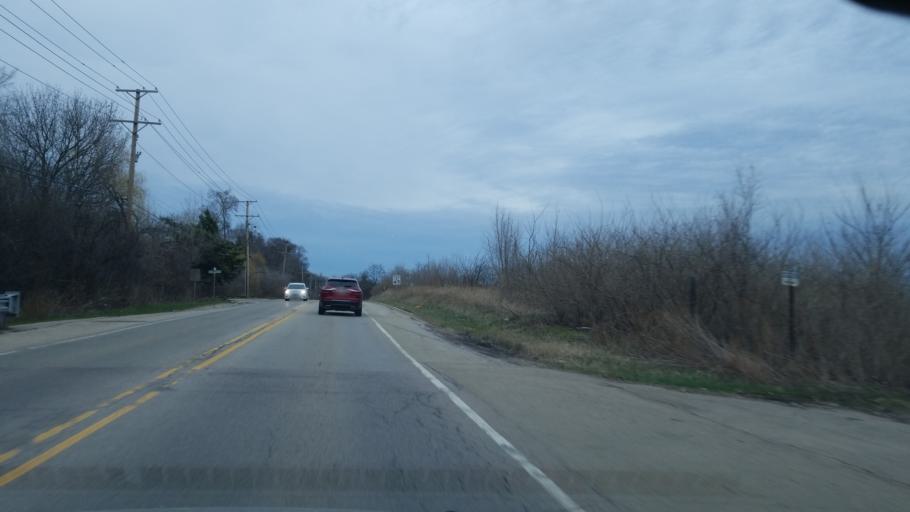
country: US
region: Illinois
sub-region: Kane County
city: Sleepy Hollow
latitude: 42.1033
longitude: -88.3286
